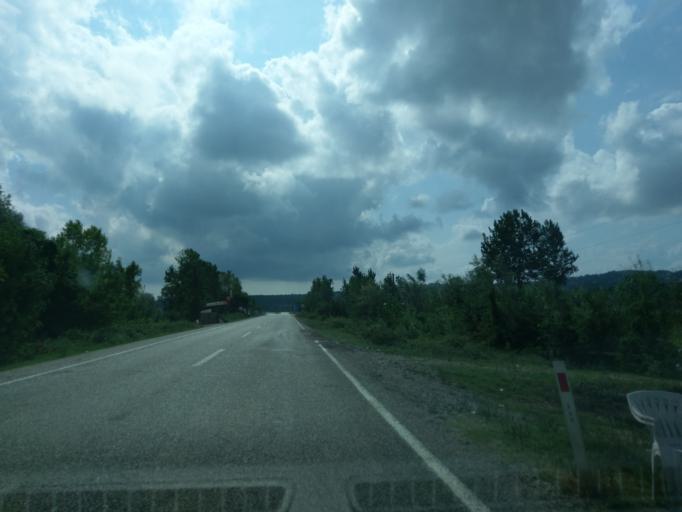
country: TR
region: Sinop
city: Sinop
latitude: 42.0150
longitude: 35.0545
